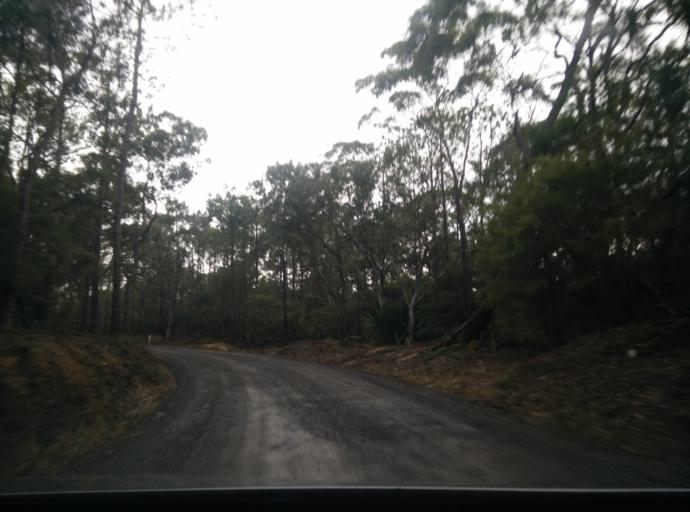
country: AU
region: New South Wales
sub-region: Gosford Shire
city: Narara
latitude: -33.3692
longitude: 151.3249
